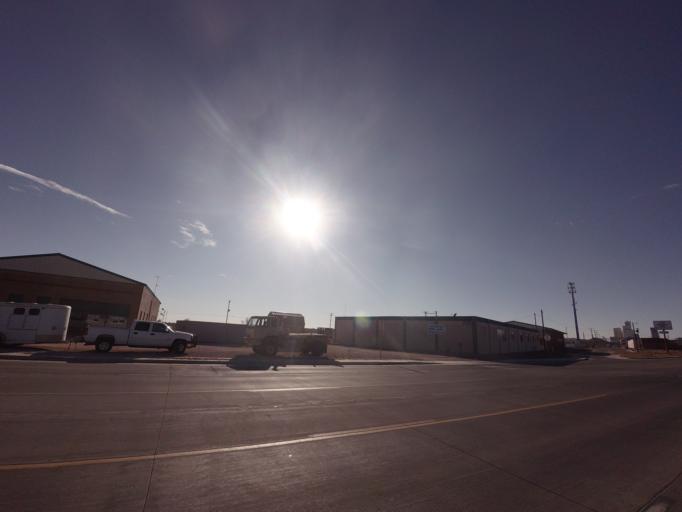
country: US
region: New Mexico
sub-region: Curry County
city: Clovis
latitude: 34.3975
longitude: -103.1875
